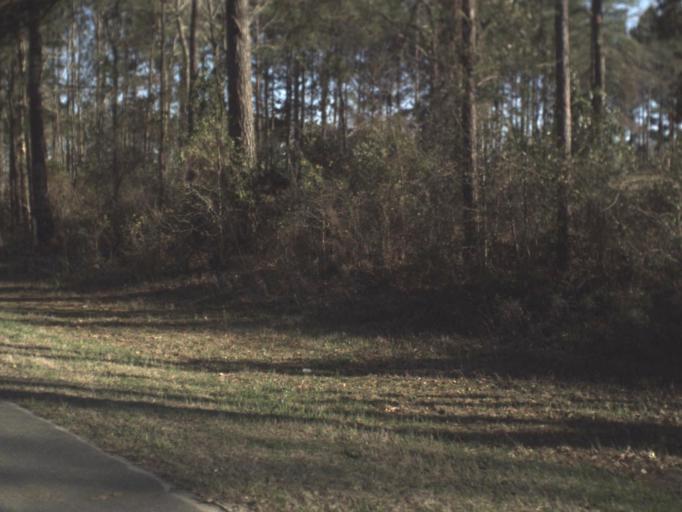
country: US
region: Florida
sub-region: Jackson County
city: Sneads
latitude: 30.7136
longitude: -84.9489
